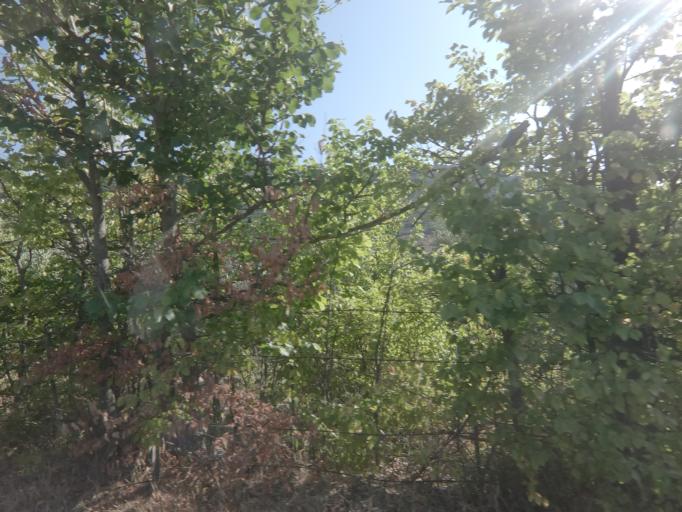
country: PT
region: Vila Real
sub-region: Sabrosa
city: Vilela
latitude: 41.1870
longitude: -7.5372
